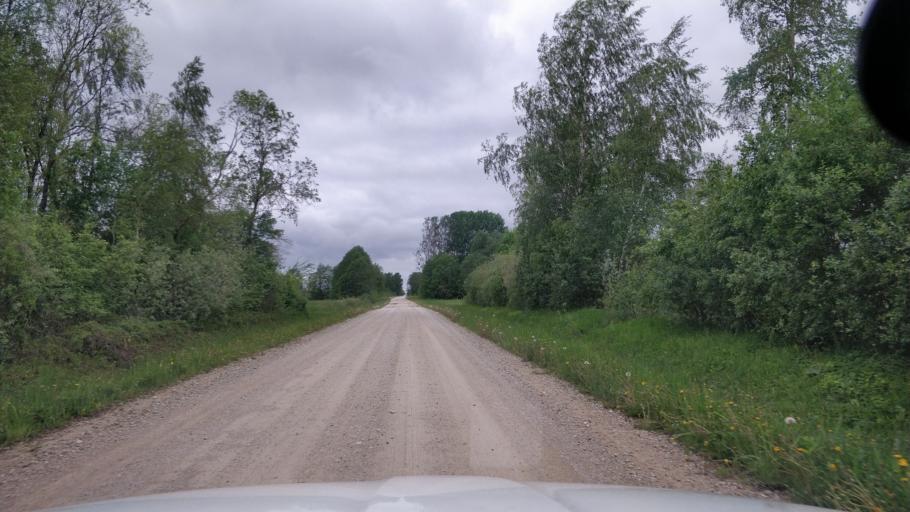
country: EE
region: Raplamaa
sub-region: Maerjamaa vald
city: Marjamaa
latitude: 58.7168
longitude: 24.2812
